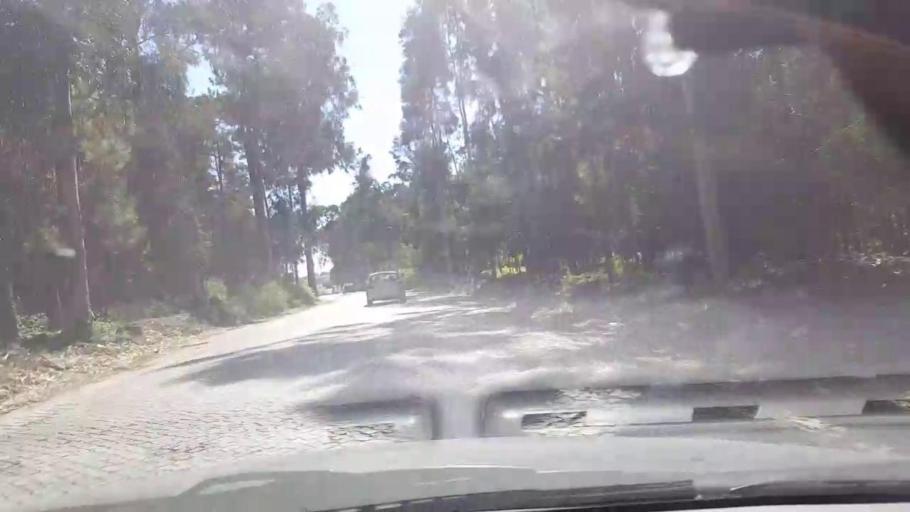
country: PT
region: Porto
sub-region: Vila do Conde
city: Arvore
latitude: 41.3224
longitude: -8.7246
